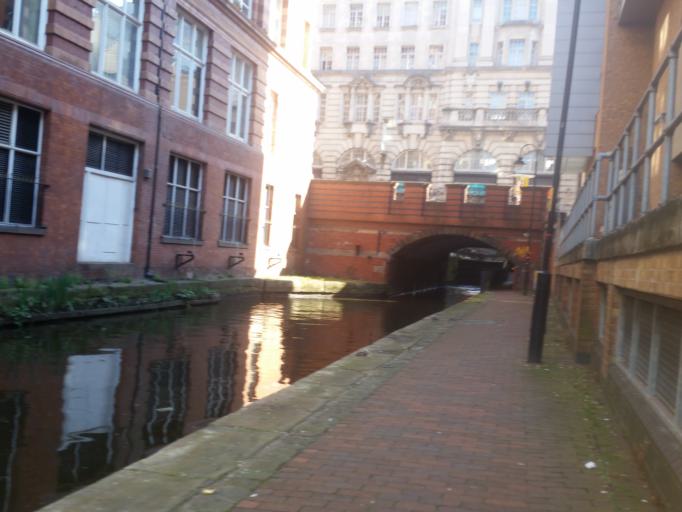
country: GB
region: England
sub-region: Manchester
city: Manchester
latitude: 53.4750
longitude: -2.2423
